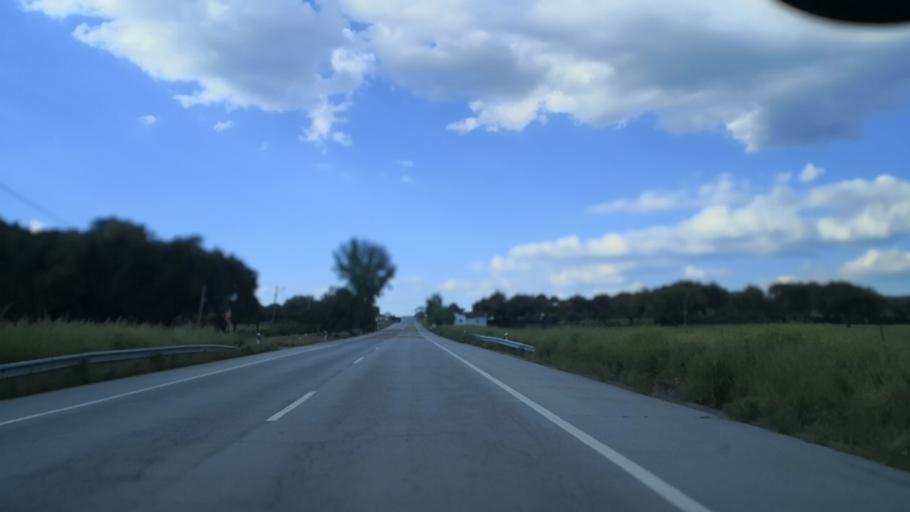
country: PT
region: Portalegre
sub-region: Portalegre
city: Urra
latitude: 39.2335
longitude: -7.4534
